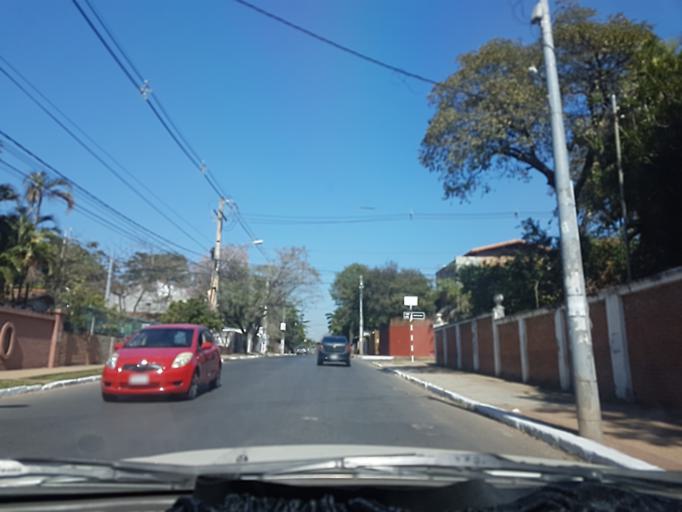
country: PY
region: Asuncion
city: Asuncion
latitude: -25.2685
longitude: -57.5932
